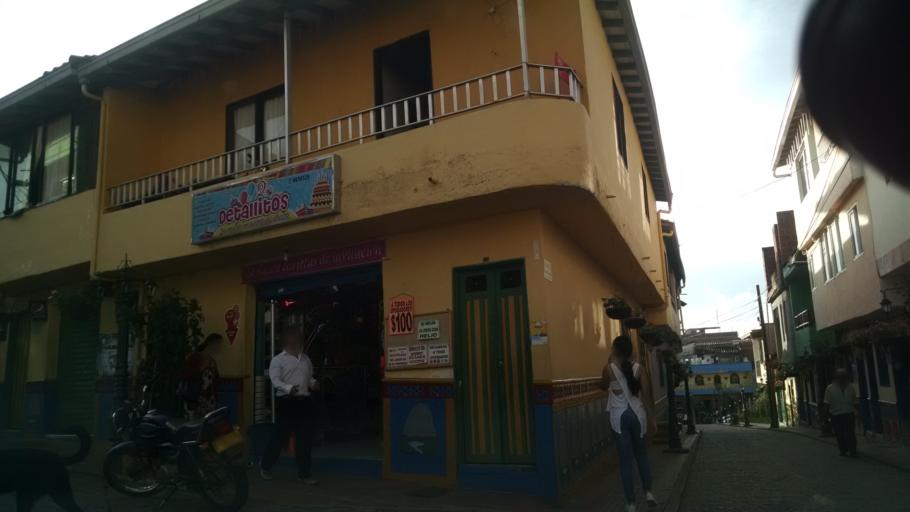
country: CO
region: Antioquia
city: Guatape
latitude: 6.2340
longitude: -75.1597
